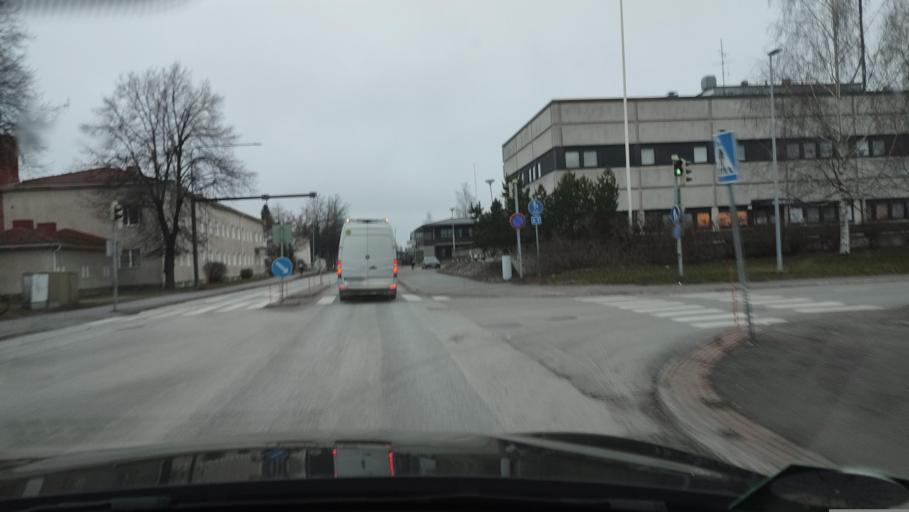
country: FI
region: Southern Ostrobothnia
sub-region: Suupohja
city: Kauhajoki
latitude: 62.4237
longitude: 22.1758
